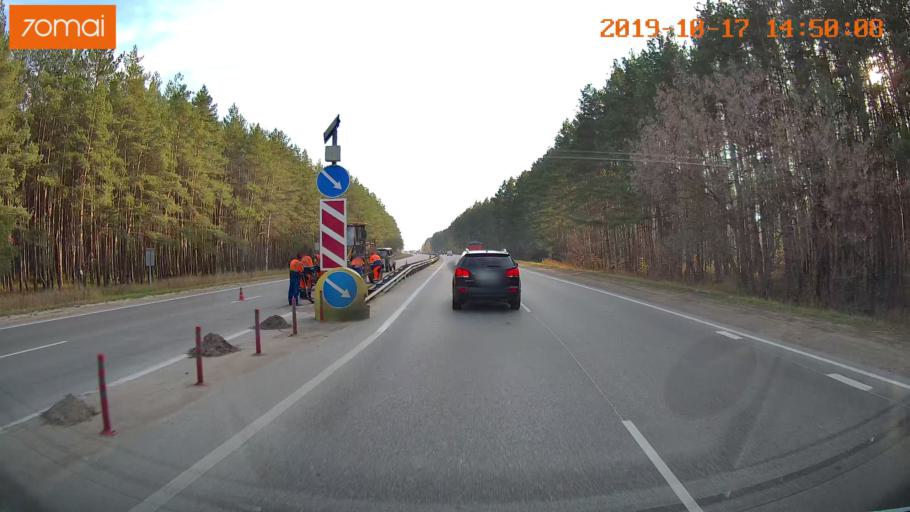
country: RU
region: Rjazan
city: Polyany
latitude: 54.7380
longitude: 39.8410
